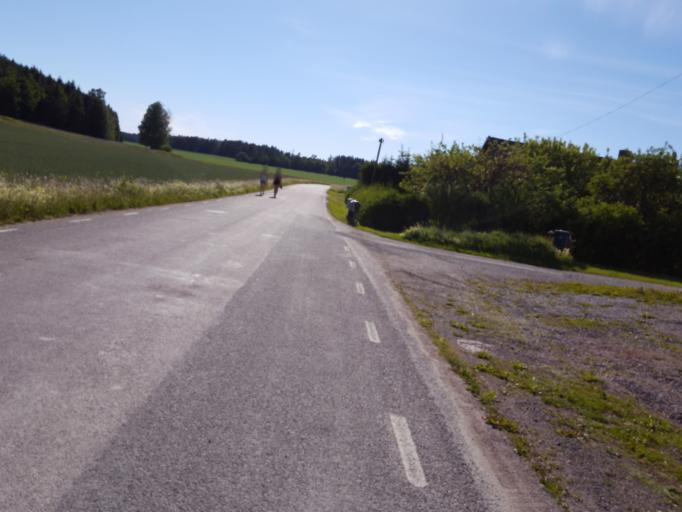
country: SE
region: Uppsala
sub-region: Uppsala Kommun
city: Saevja
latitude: 59.8269
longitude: 17.7720
